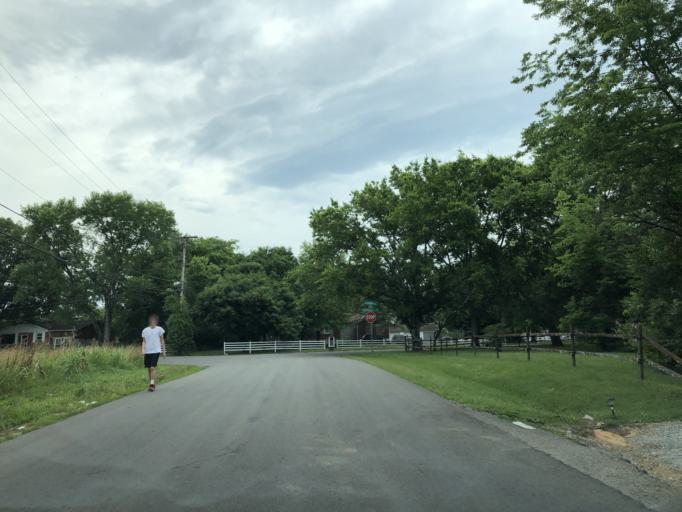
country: US
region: Tennessee
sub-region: Davidson County
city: Goodlettsville
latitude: 36.2832
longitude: -86.7053
